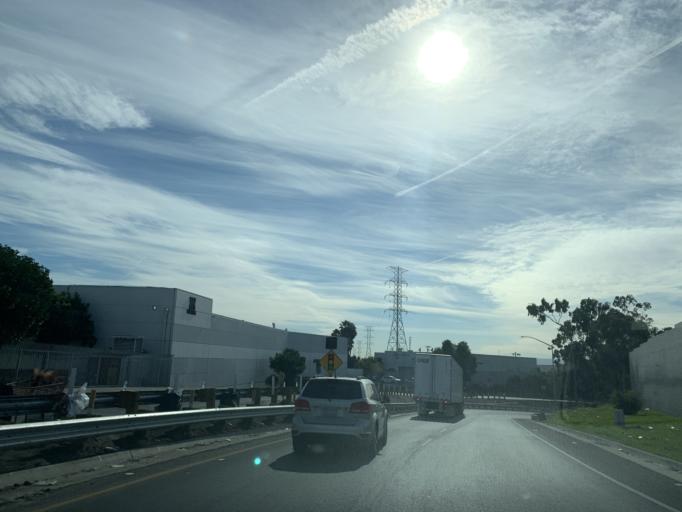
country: US
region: California
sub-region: Los Angeles County
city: West Athens
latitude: 33.9162
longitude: -118.2847
